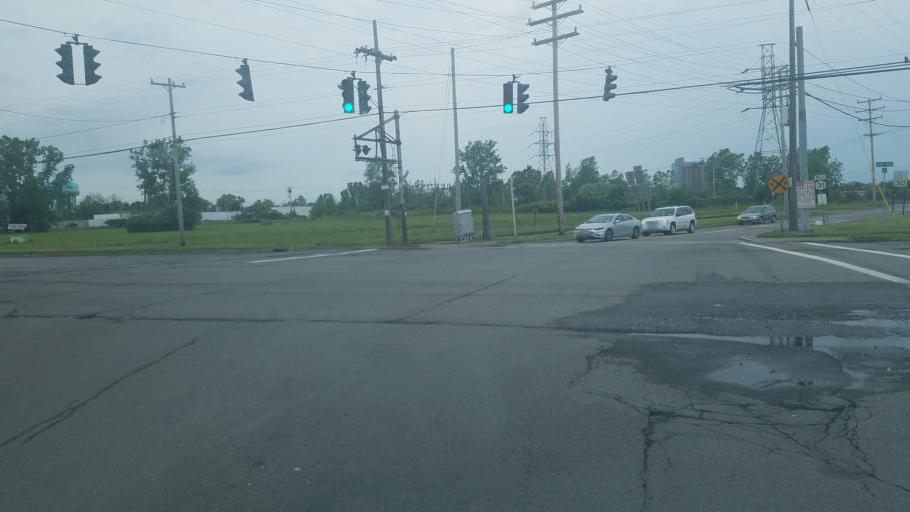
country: US
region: New York
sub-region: Niagara County
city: Niagara Falls
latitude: 43.1220
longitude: -79.0357
